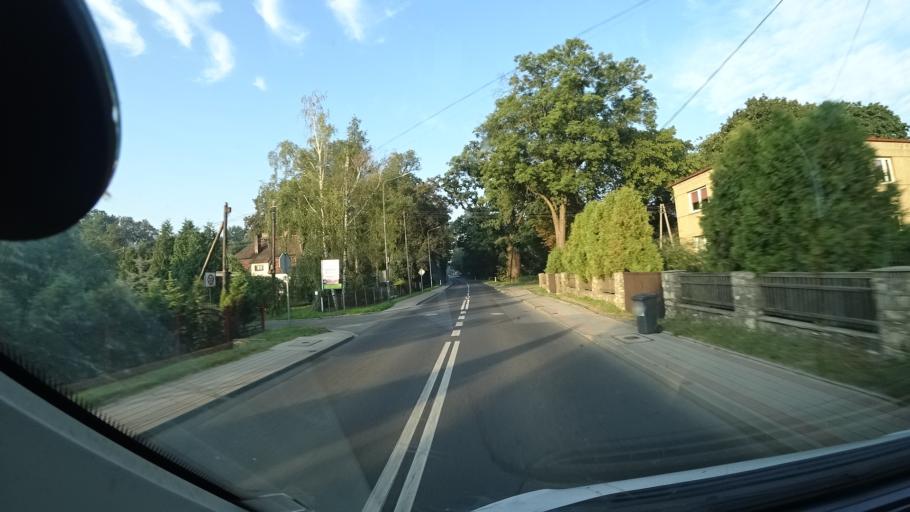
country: PL
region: Opole Voivodeship
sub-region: Powiat kedzierzynsko-kozielski
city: Slawiecice
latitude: 50.3715
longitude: 18.3200
